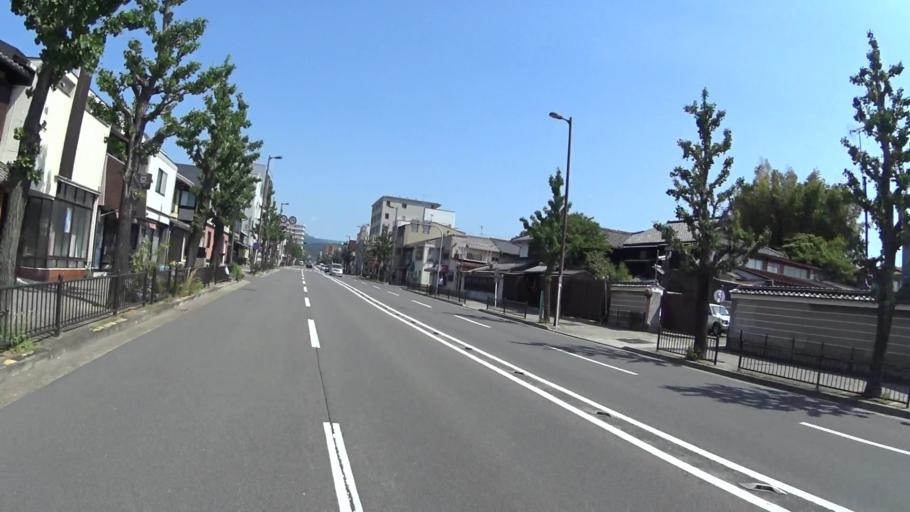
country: JP
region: Kyoto
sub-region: Kyoto-shi
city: Kamigyo-ku
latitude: 35.0352
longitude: 135.7593
